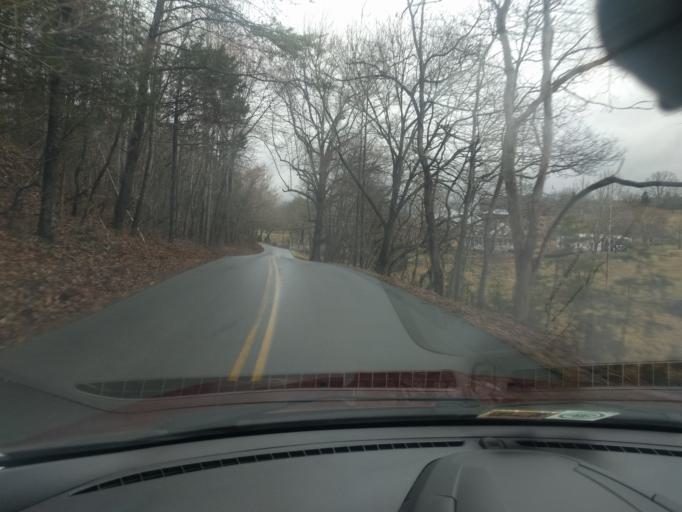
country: US
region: Virginia
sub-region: Botetourt County
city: Fincastle
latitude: 37.5595
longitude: -79.8789
